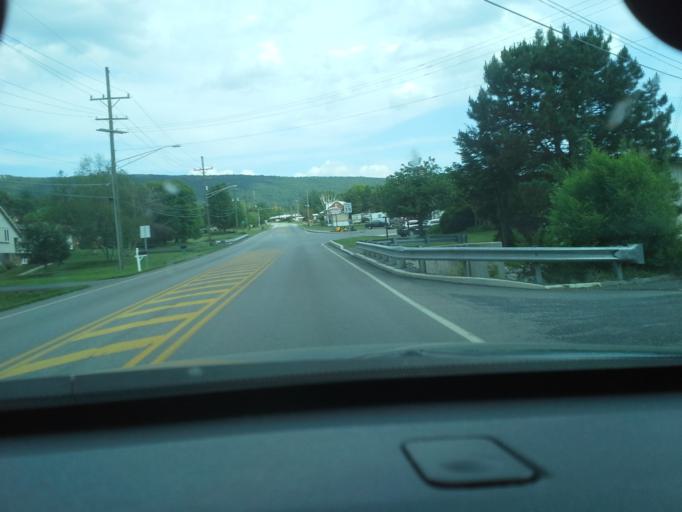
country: US
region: Pennsylvania
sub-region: Fulton County
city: McConnellsburg
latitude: 39.9257
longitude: -77.9858
